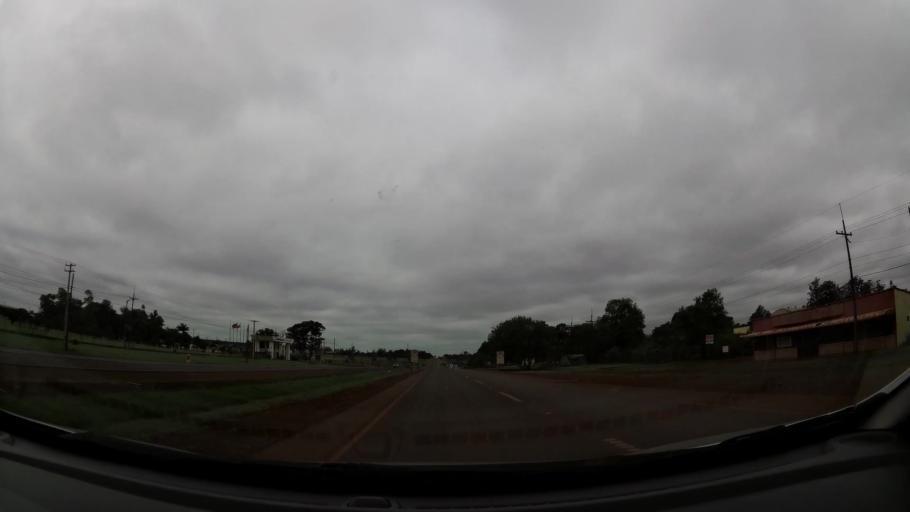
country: PY
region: Alto Parana
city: Colonia Yguazu
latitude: -25.4878
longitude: -54.8352
